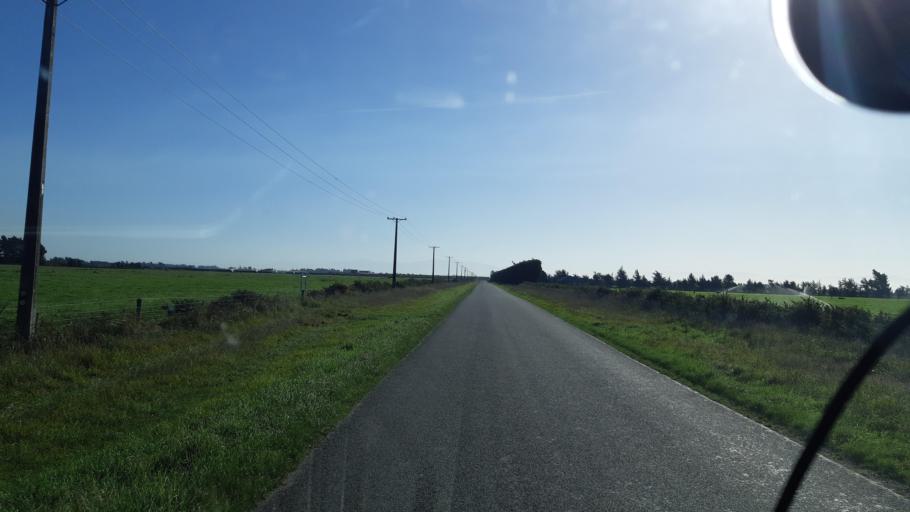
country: NZ
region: Canterbury
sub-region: Selwyn District
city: Burnham
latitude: -43.6327
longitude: 172.2170
